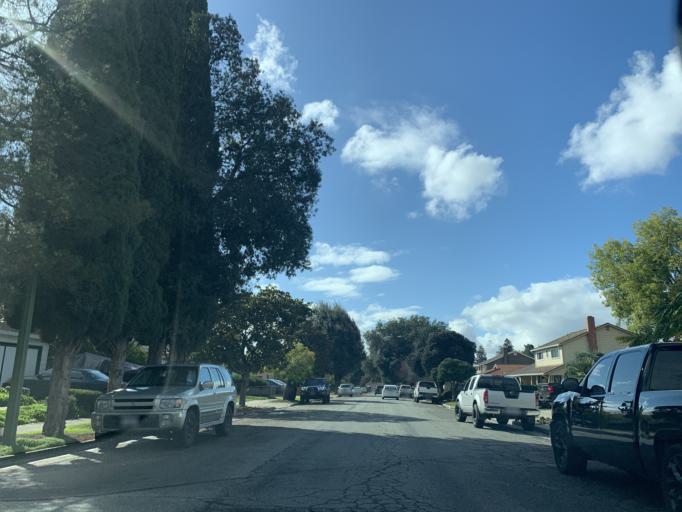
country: US
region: California
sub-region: Santa Clara County
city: Milpitas
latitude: 37.3978
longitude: -121.8683
